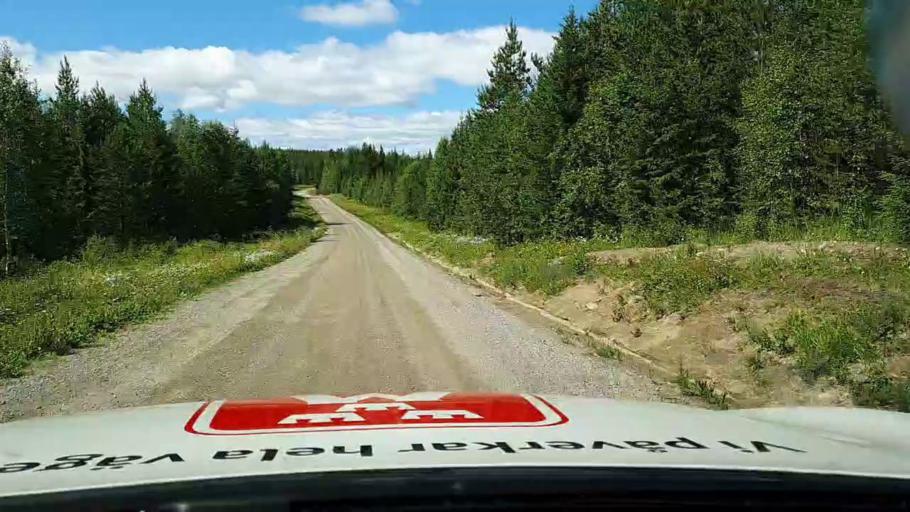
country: SE
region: Jaemtland
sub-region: Braecke Kommun
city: Braecke
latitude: 62.7353
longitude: 15.4825
